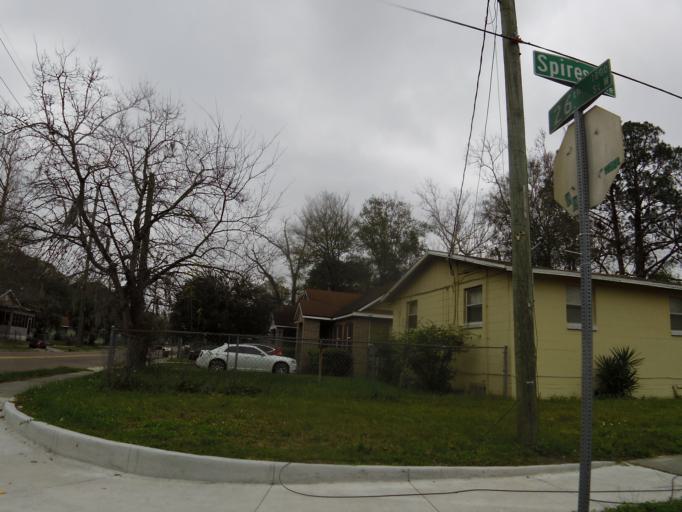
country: US
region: Florida
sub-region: Duval County
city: Jacksonville
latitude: 30.3599
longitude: -81.6882
